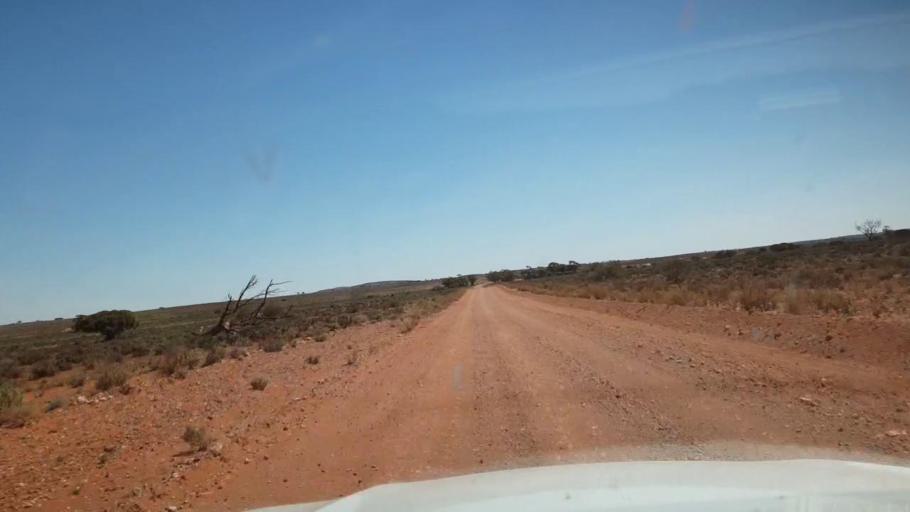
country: AU
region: South Australia
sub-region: Whyalla
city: Whyalla
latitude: -32.6834
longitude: 137.0950
